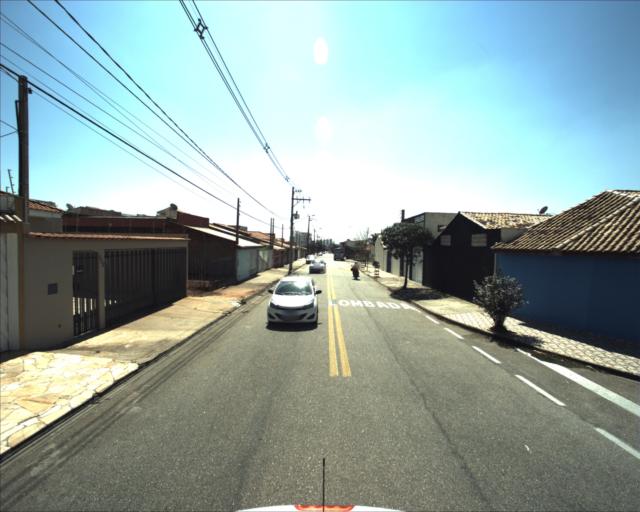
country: BR
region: Sao Paulo
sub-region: Sorocaba
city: Sorocaba
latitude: -23.5107
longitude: -47.5133
